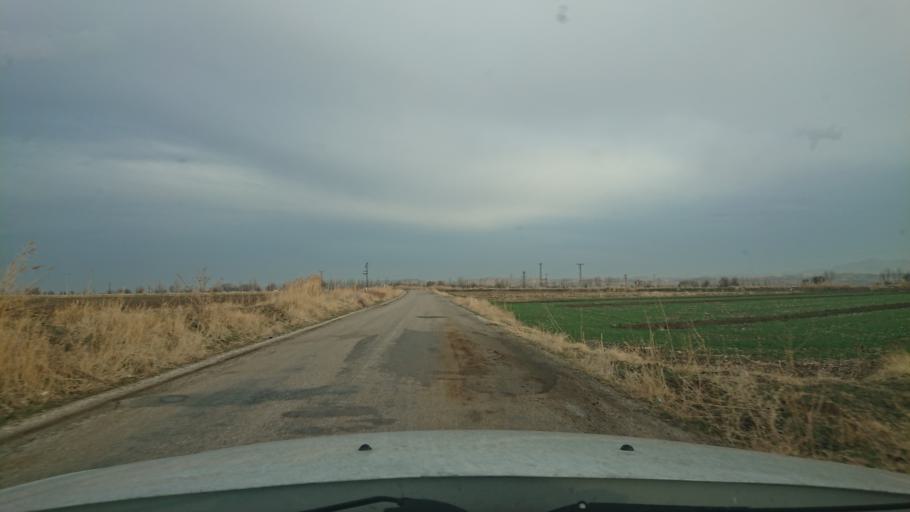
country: TR
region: Aksaray
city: Yesilova
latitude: 38.4367
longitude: 33.8381
